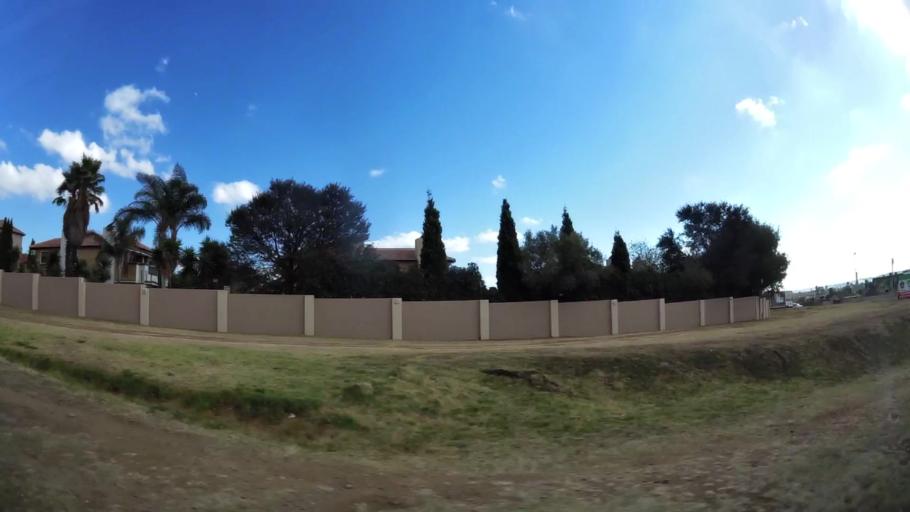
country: ZA
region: Gauteng
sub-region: West Rand District Municipality
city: Muldersdriseloop
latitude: -26.0792
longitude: 27.8580
